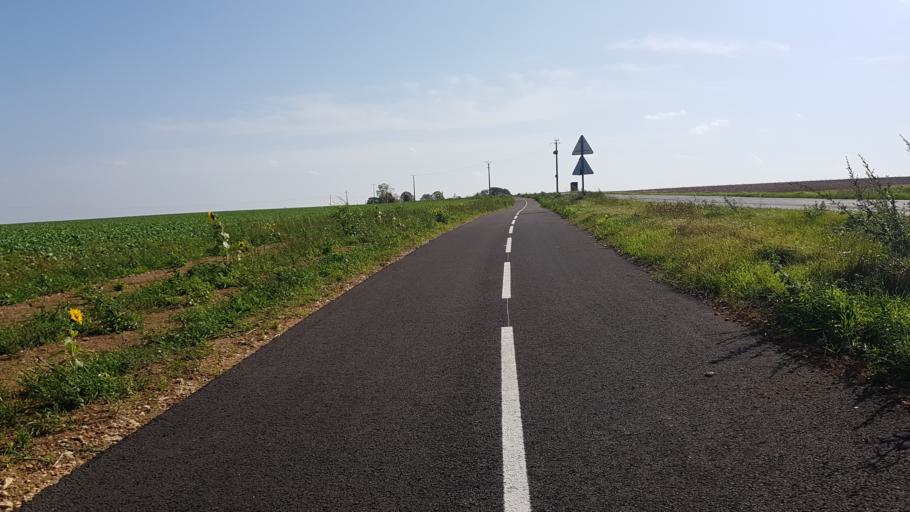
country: FR
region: Poitou-Charentes
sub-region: Departement de la Vienne
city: Chasseneuil-du-Poitou
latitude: 46.6595
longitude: 0.3442
